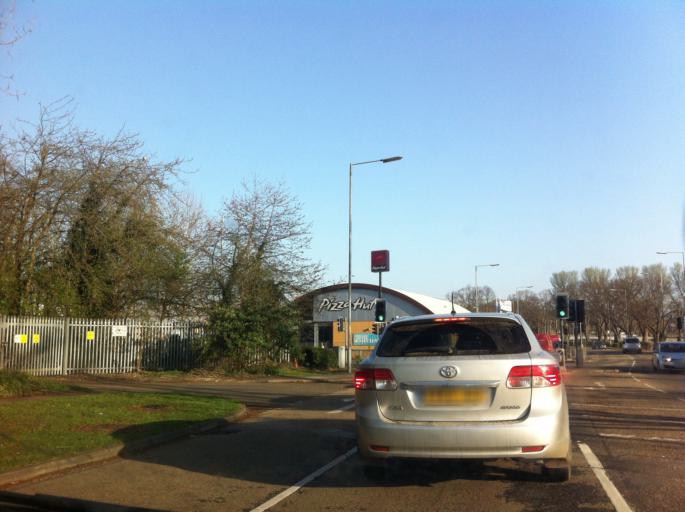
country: GB
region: England
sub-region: Northamptonshire
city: Wellingborough
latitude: 52.2924
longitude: -0.6838
